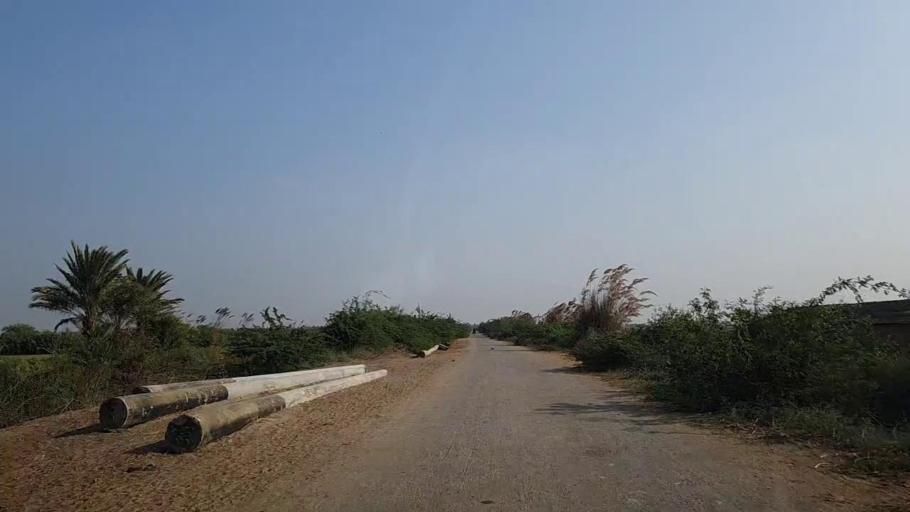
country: PK
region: Sindh
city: Mirpur Sakro
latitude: 24.6262
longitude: 67.6540
